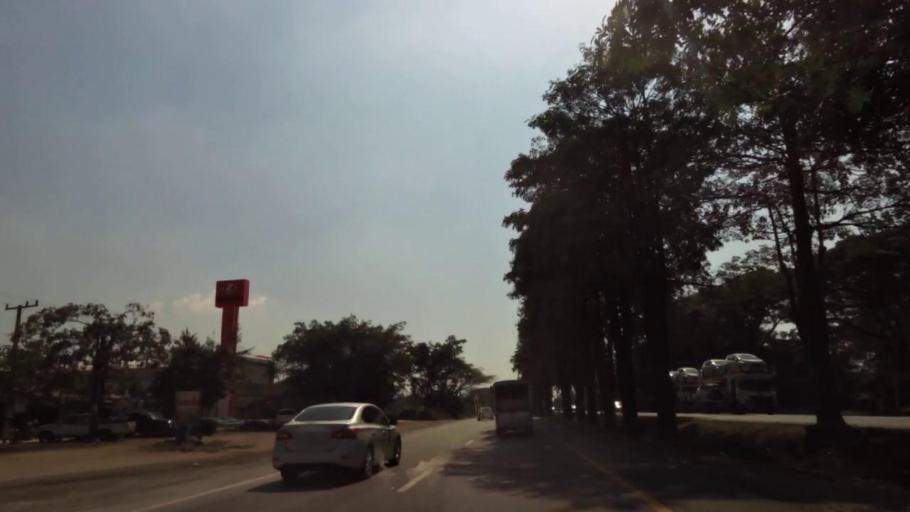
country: TH
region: Phichit
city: Bueng Na Rang
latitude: 16.1177
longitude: 100.1257
